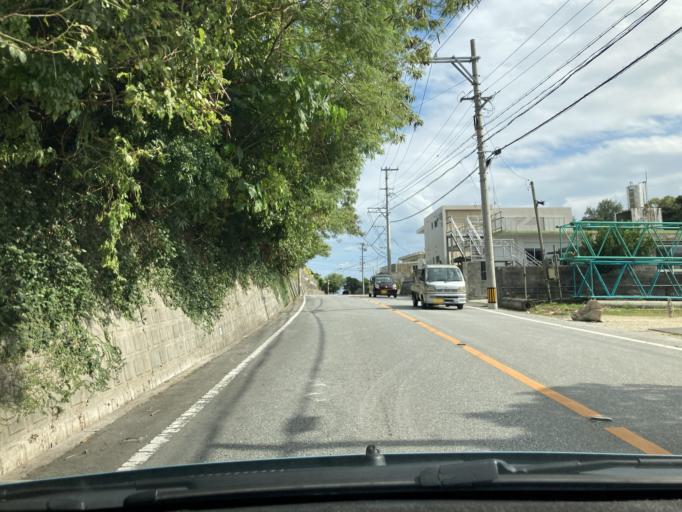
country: JP
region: Okinawa
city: Ginowan
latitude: 26.2690
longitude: 127.7851
